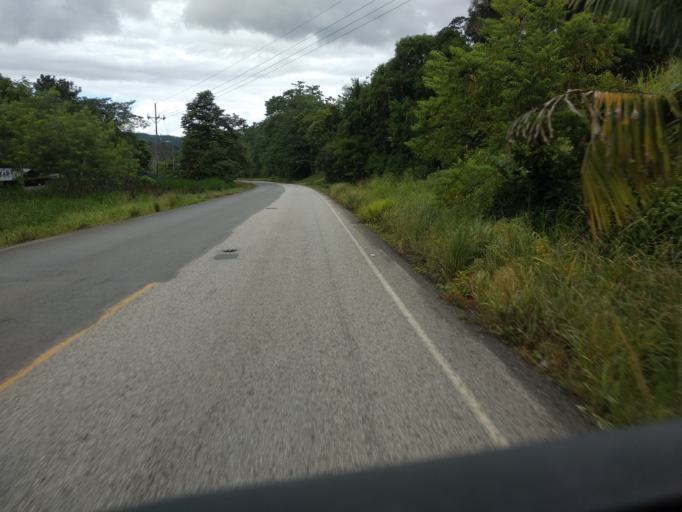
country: CR
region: Puntarenas
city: Buenos Aires
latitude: 9.1078
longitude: -83.2861
